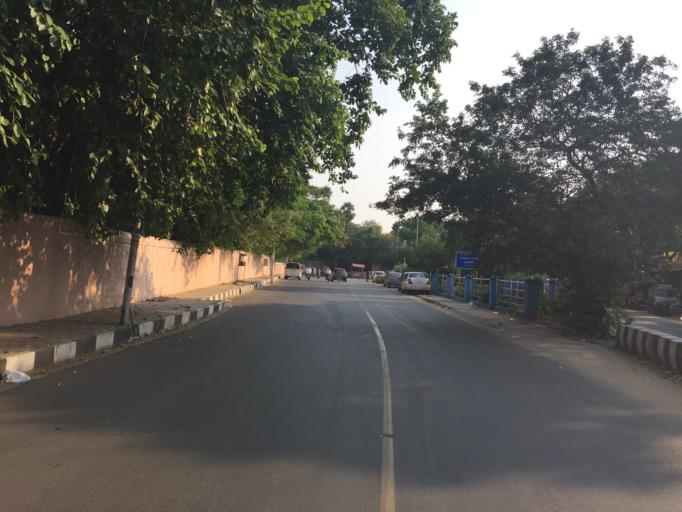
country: IN
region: Tamil Nadu
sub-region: Chennai
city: Gandhi Nagar
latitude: 13.0213
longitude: 80.2631
